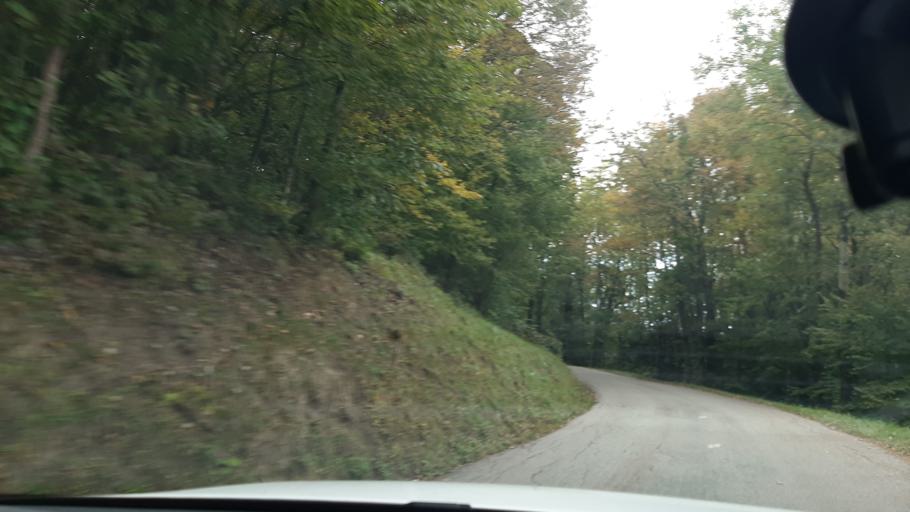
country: FR
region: Rhone-Alpes
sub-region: Departement de la Savoie
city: Villargondran
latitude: 45.2536
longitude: 6.3628
